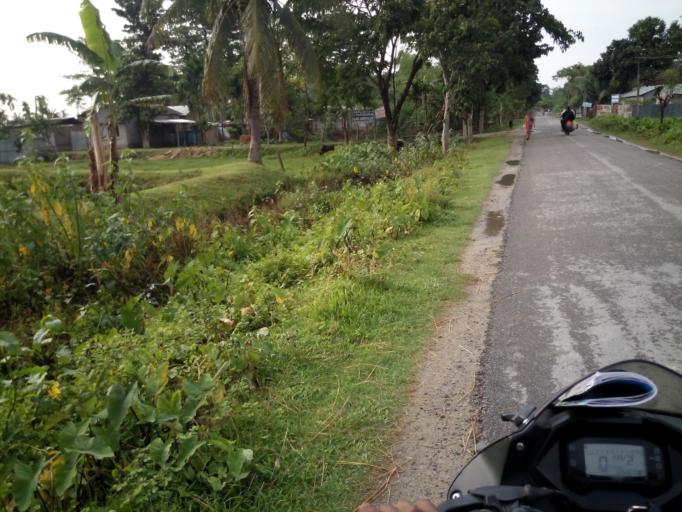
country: IN
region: Assam
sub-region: Darrang
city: Kharupatia
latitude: 26.6178
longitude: 92.2904
